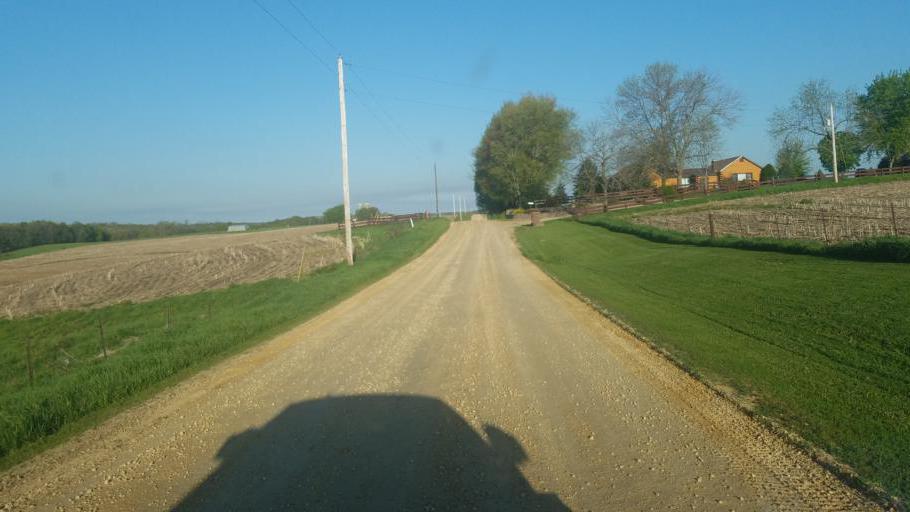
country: US
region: Wisconsin
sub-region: Vernon County
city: Hillsboro
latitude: 43.5673
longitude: -90.5220
